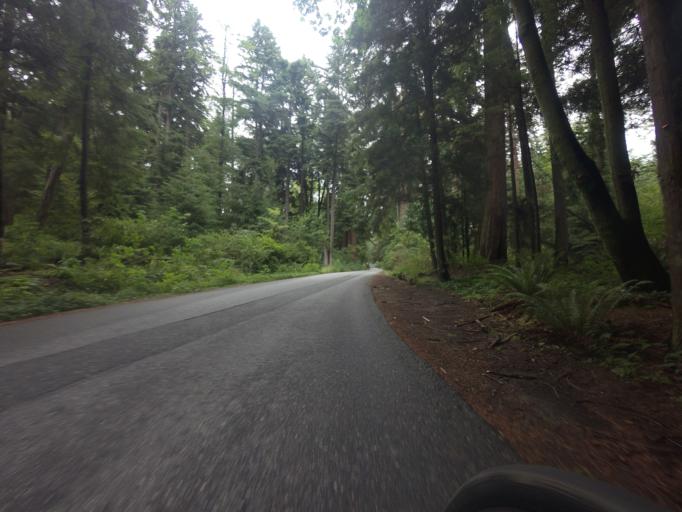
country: CA
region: British Columbia
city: West End
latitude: 49.3103
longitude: -123.1444
